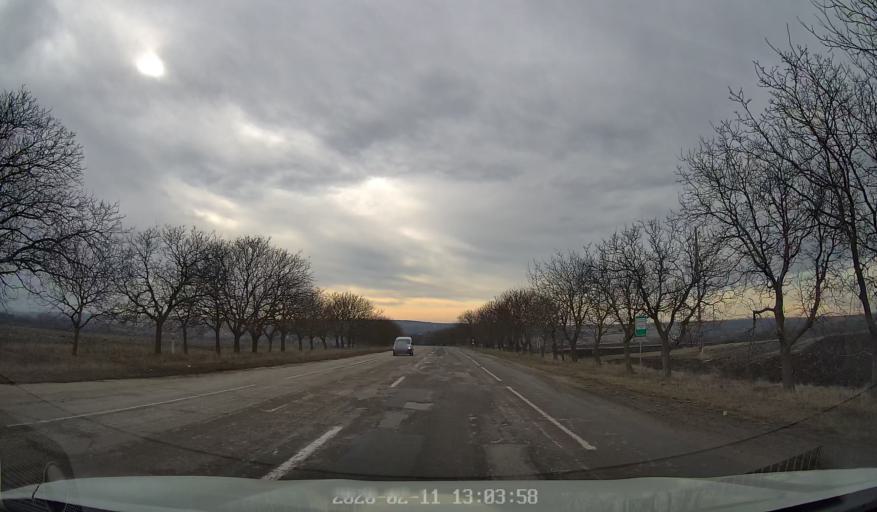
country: MD
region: Briceni
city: Briceni
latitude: 48.3076
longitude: 26.9498
